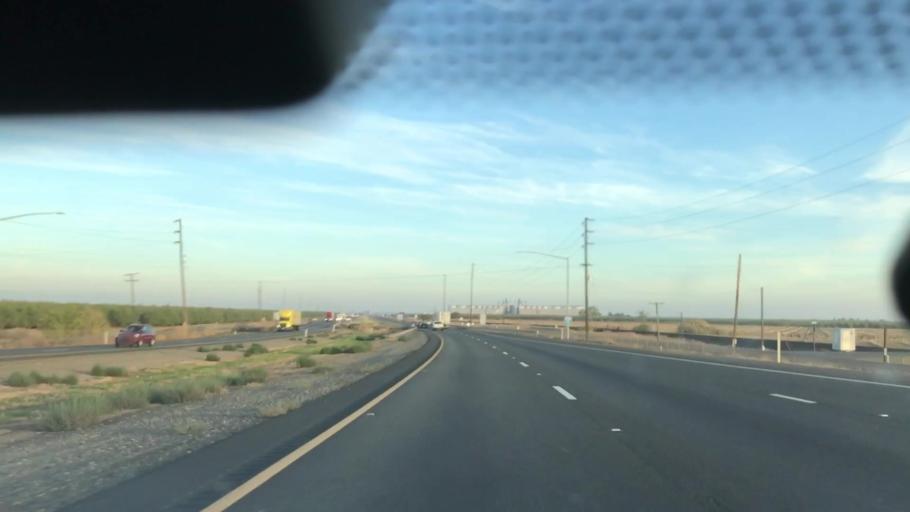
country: US
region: California
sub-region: Colusa County
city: Arbuckle
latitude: 39.0267
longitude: -122.0634
